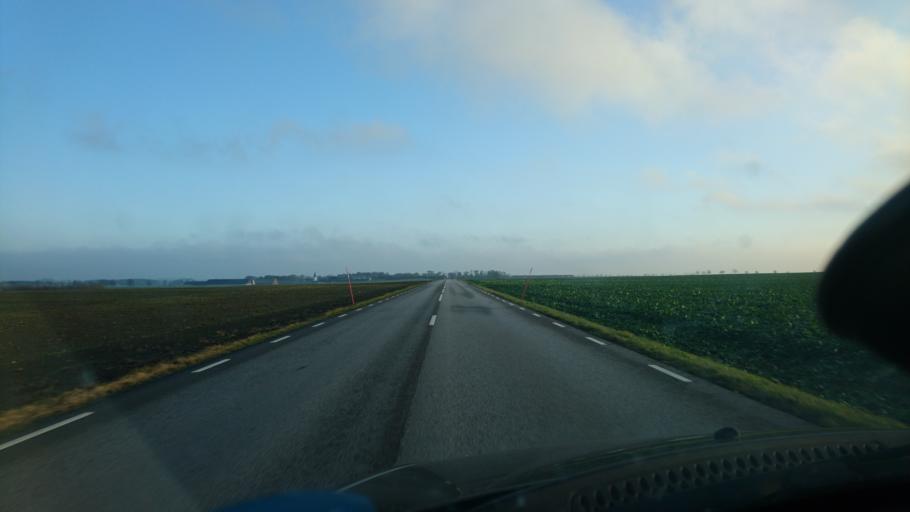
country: SE
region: Skane
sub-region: Tomelilla Kommun
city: Tomelilla
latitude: 55.5008
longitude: 14.0338
